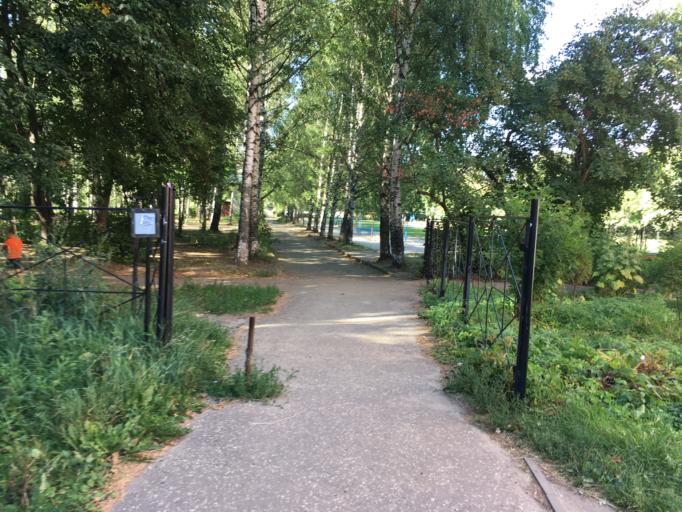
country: RU
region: Mariy-El
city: Yoshkar-Ola
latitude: 56.6431
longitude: 47.8683
